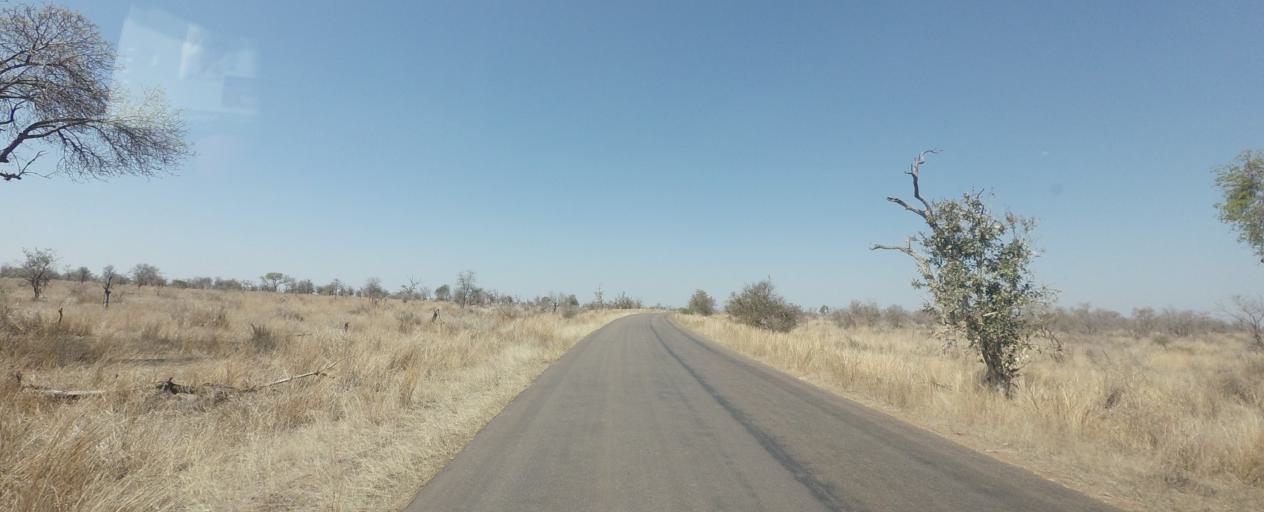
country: ZA
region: Limpopo
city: Thulamahashi
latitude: -24.3897
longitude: 31.7226
